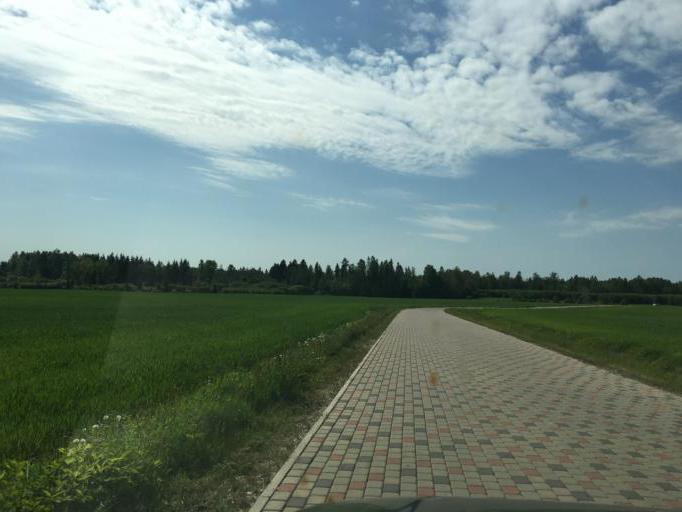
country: LV
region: Talsu Rajons
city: Valdemarpils
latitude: 57.3773
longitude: 22.5208
